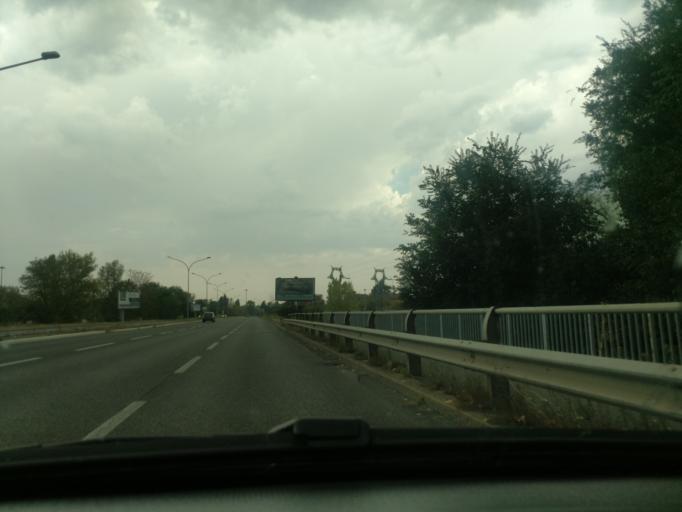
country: IT
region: Emilia-Romagna
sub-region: Provincia di Bologna
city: Casalecchio di Reno
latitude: 44.5058
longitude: 11.2881
